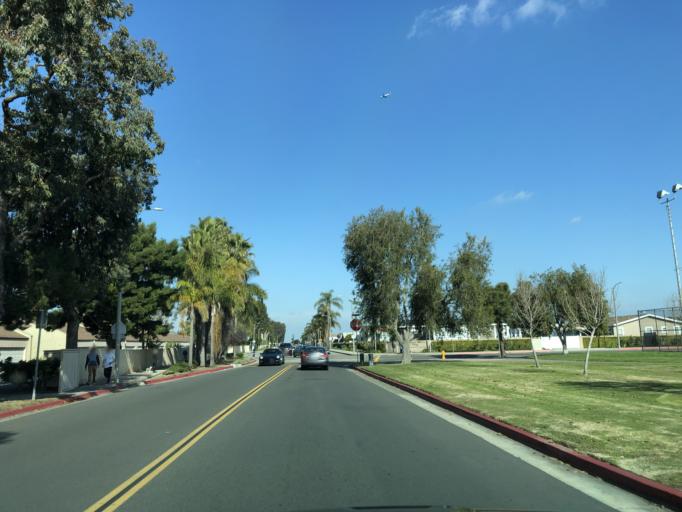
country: US
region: California
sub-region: Orange County
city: Seal Beach
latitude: 33.7220
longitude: -118.0545
